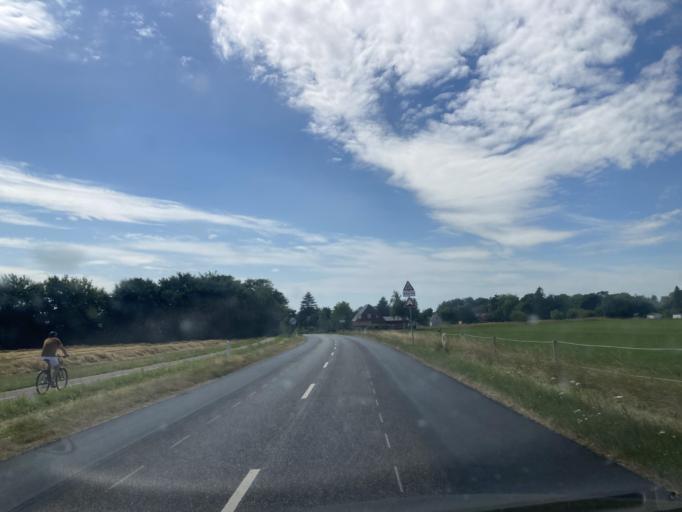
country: DK
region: Zealand
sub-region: Solrod Kommune
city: Solrod
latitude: 55.5292
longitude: 12.1686
